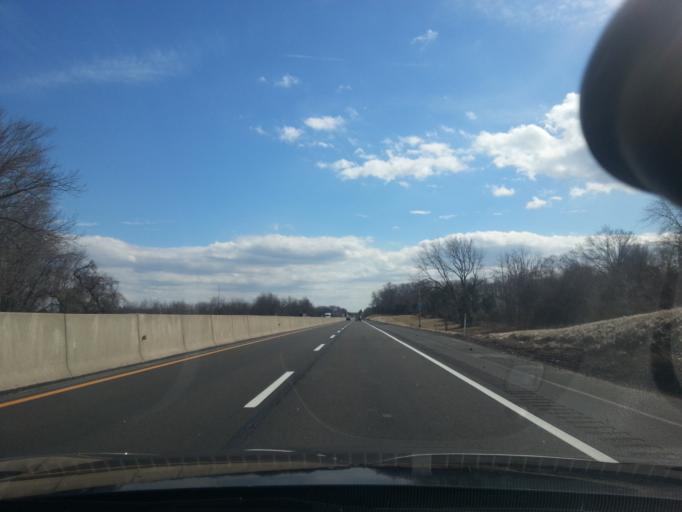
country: US
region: Pennsylvania
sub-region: Montgomery County
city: Harleysville
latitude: 40.3173
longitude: -75.3762
